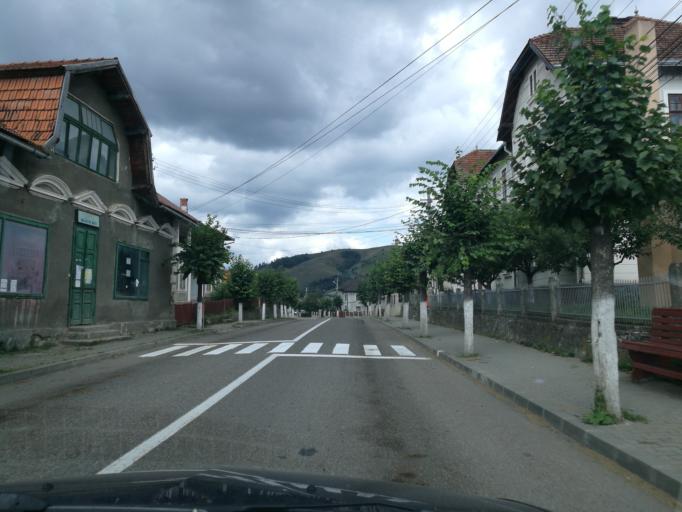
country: RO
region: Suceava
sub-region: Comuna Frumosu
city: Frumosu
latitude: 47.6090
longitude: 25.6469
